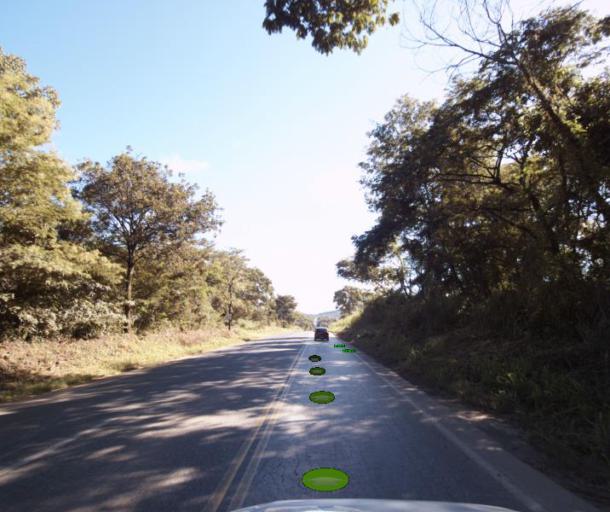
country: BR
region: Goias
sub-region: Uruacu
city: Uruacu
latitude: -14.5982
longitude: -49.1645
